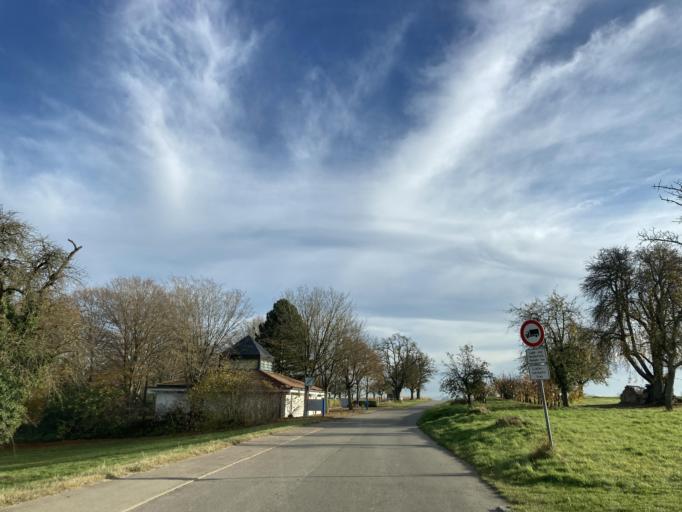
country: DE
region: Baden-Wuerttemberg
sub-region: Regierungsbezirk Stuttgart
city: Bondorf
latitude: 48.4710
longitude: 8.8214
